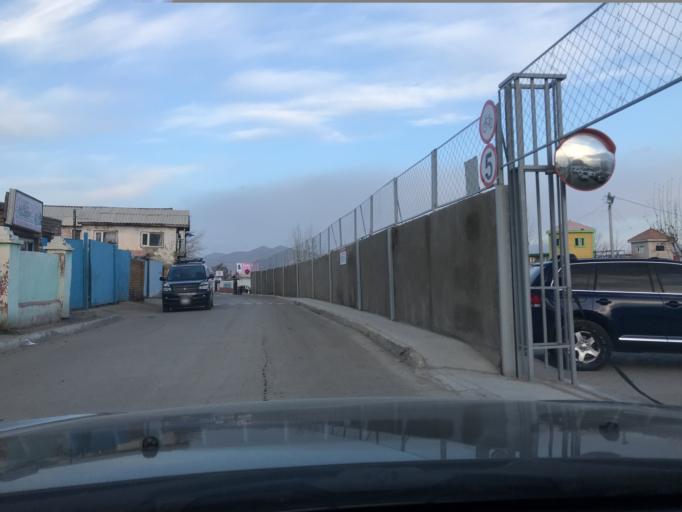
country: MN
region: Ulaanbaatar
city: Ulaanbaatar
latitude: 47.9299
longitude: 106.9979
